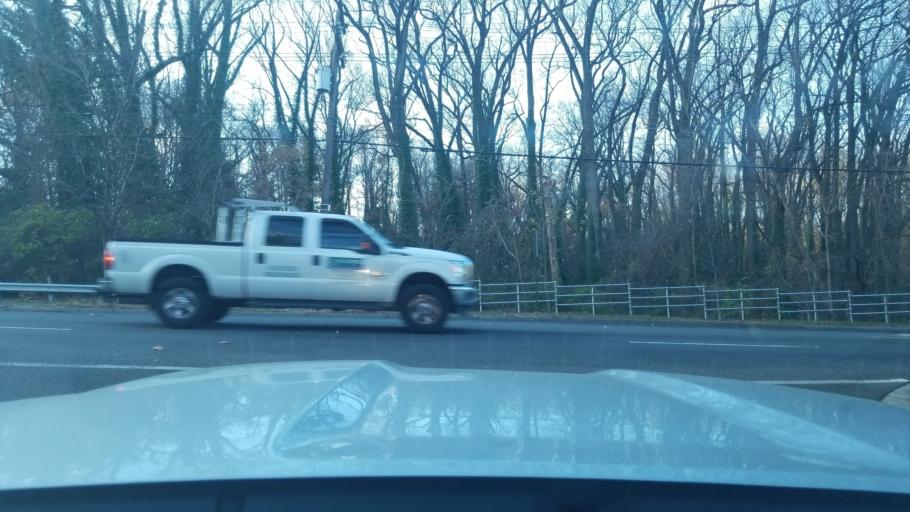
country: US
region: Maryland
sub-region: Prince George's County
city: Silver Hill
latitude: 38.8666
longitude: -76.9532
